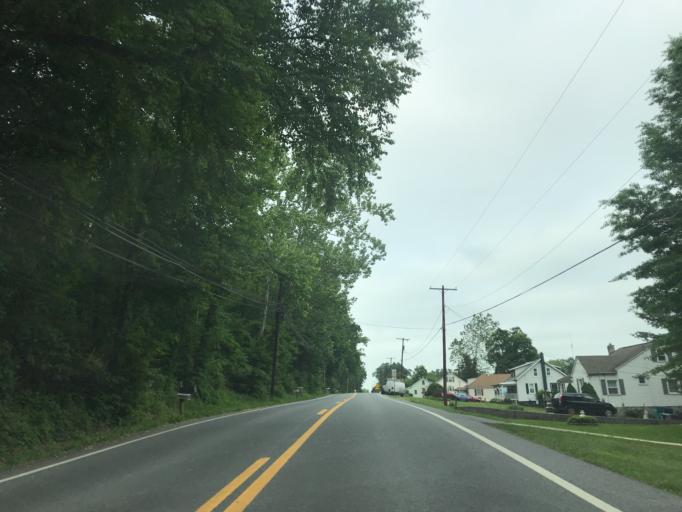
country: US
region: Maryland
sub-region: Frederick County
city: Thurmont
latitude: 39.6005
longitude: -77.4270
